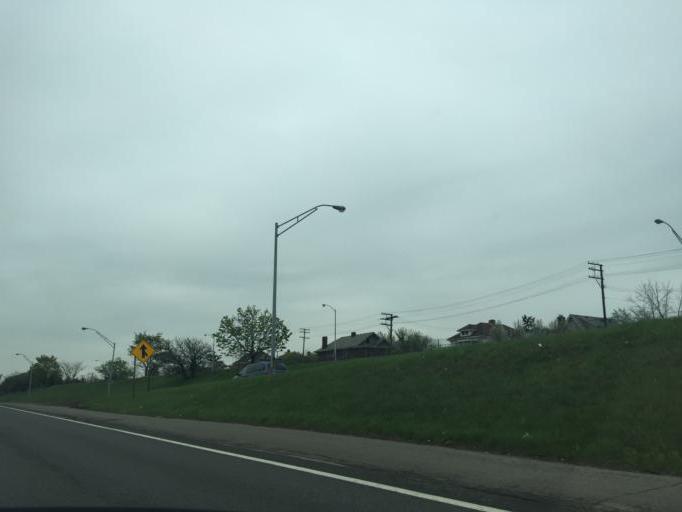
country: US
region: Michigan
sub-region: Wayne County
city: Highland Park
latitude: 42.3665
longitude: -83.1369
